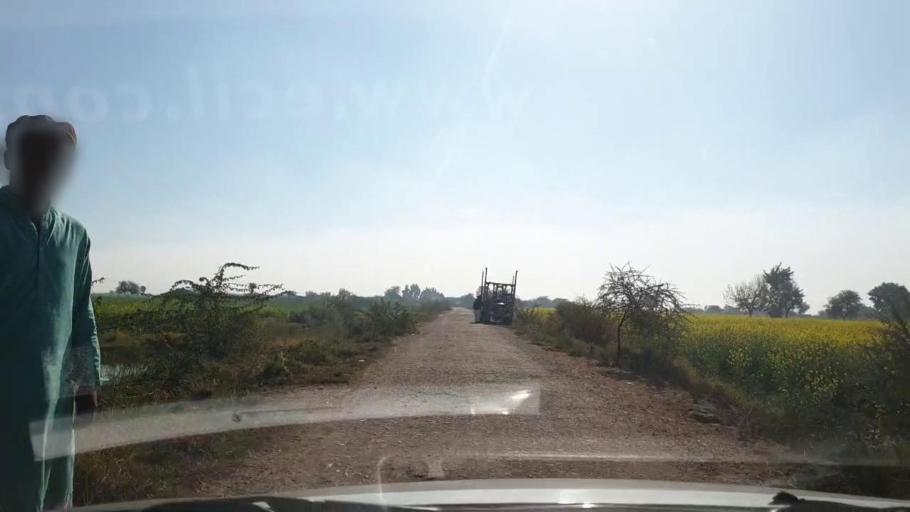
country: PK
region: Sindh
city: Jhol
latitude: 25.8134
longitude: 68.9711
